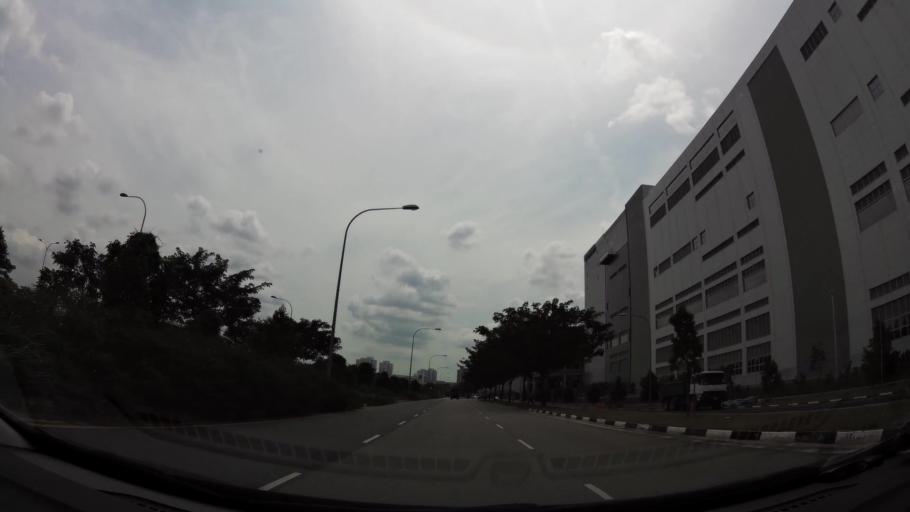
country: MY
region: Johor
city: Johor Bahru
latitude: 1.3560
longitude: 103.7090
